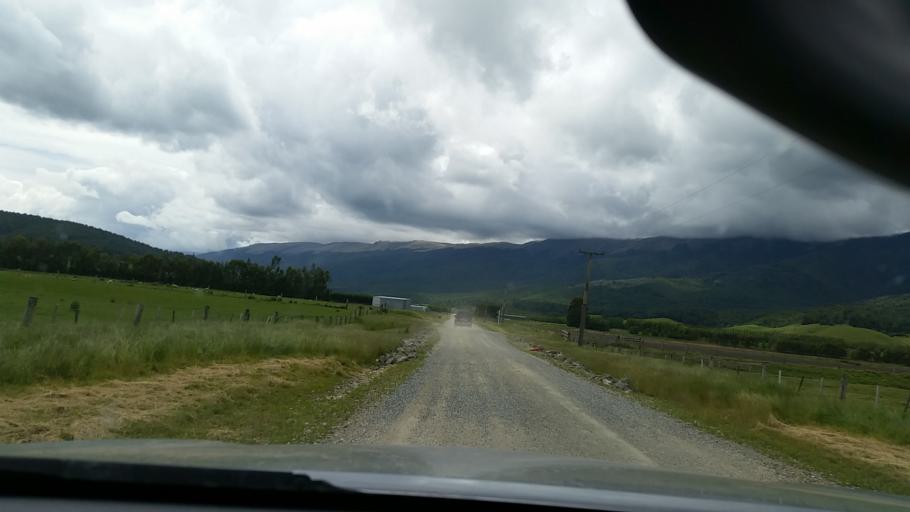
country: NZ
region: Otago
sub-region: Queenstown-Lakes District
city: Kingston
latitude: -45.6058
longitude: 168.9585
